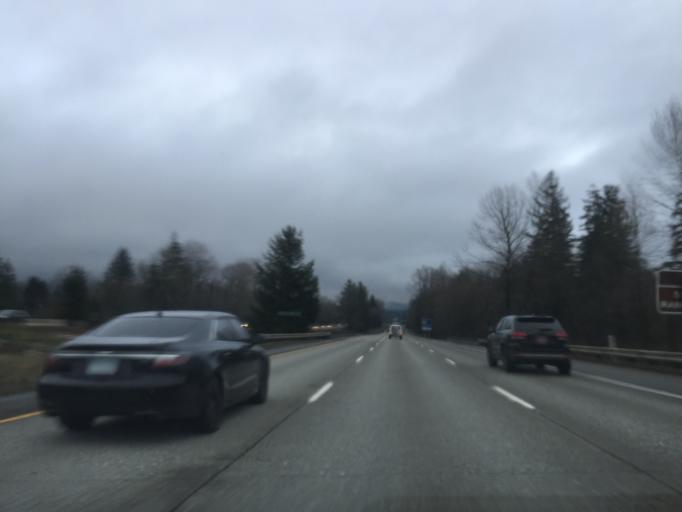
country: US
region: Washington
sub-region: King County
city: North Bend
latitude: 47.4732
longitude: -121.7760
